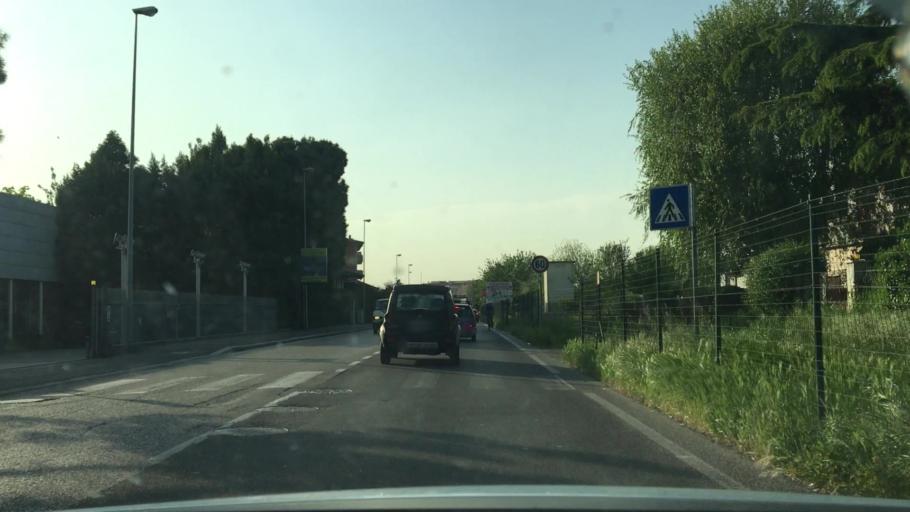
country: IT
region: Veneto
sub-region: Provincia di Verona
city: Verona
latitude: 45.4105
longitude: 11.0029
